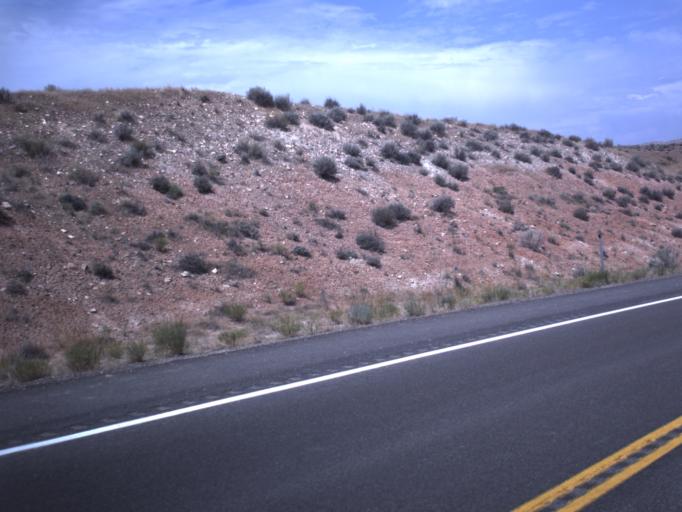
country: US
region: Utah
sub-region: Uintah County
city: Naples
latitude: 40.3031
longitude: -109.4793
